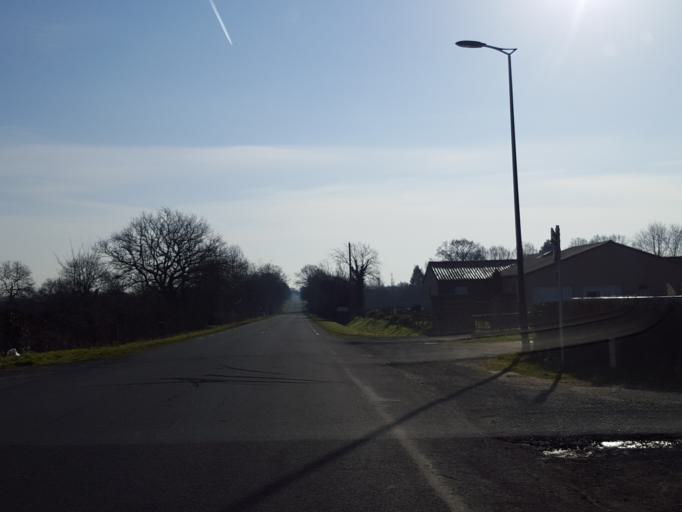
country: FR
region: Pays de la Loire
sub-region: Departement de la Vendee
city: La Chaize-le-Vicomte
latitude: 46.6688
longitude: -1.2864
